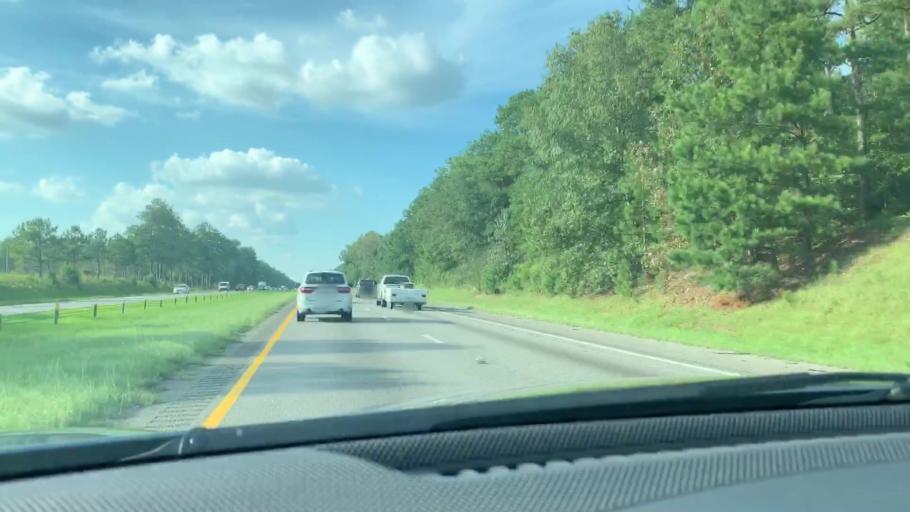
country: US
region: South Carolina
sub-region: Orangeburg County
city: Brookdale
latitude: 33.5347
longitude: -80.8042
